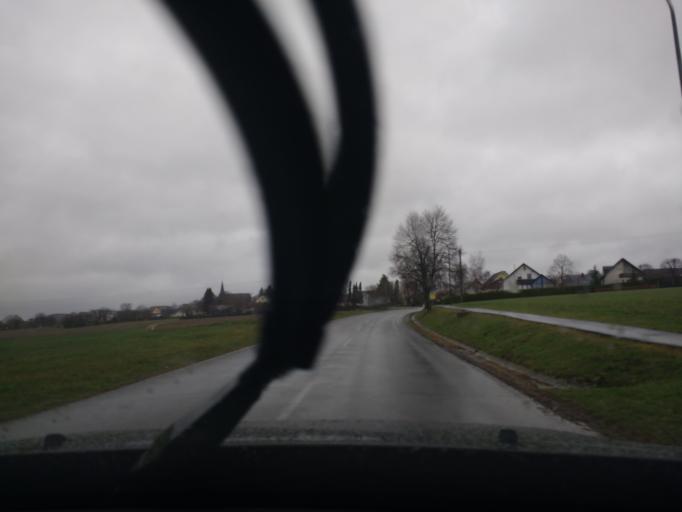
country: DE
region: Rheinland-Pfalz
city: Irmenach
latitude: 49.9190
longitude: 7.1877
